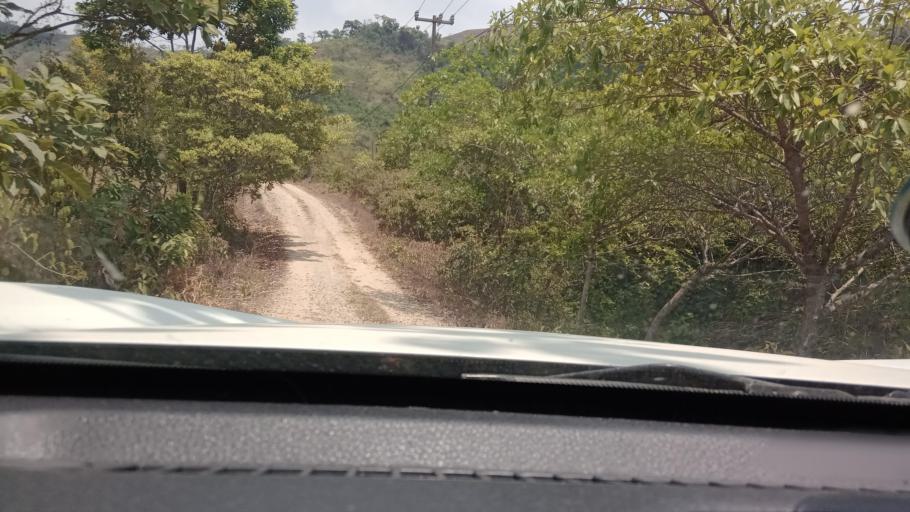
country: MX
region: Tabasco
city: Chontalpa
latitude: 17.5495
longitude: -93.7416
